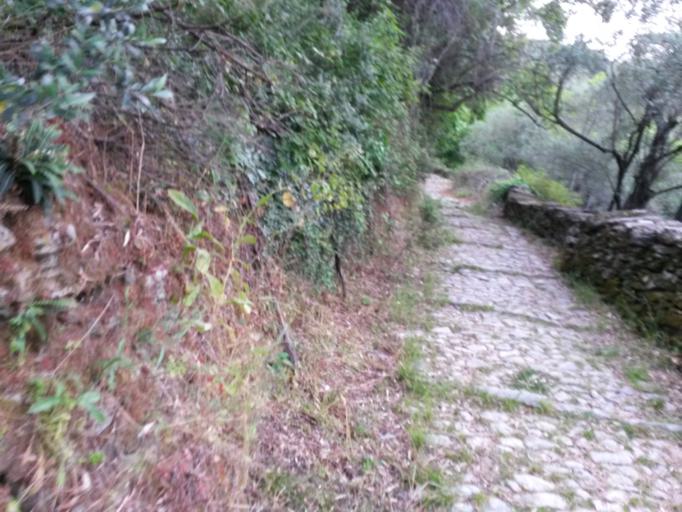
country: GR
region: North Aegean
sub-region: Nomos Lesvou
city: Agiasos
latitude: 39.0987
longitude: 26.3918
